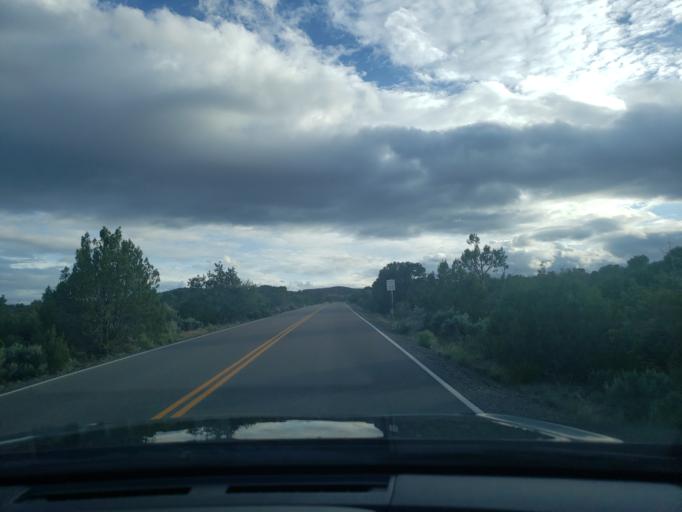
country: US
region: Colorado
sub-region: Mesa County
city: Redlands
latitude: 39.0330
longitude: -108.6510
